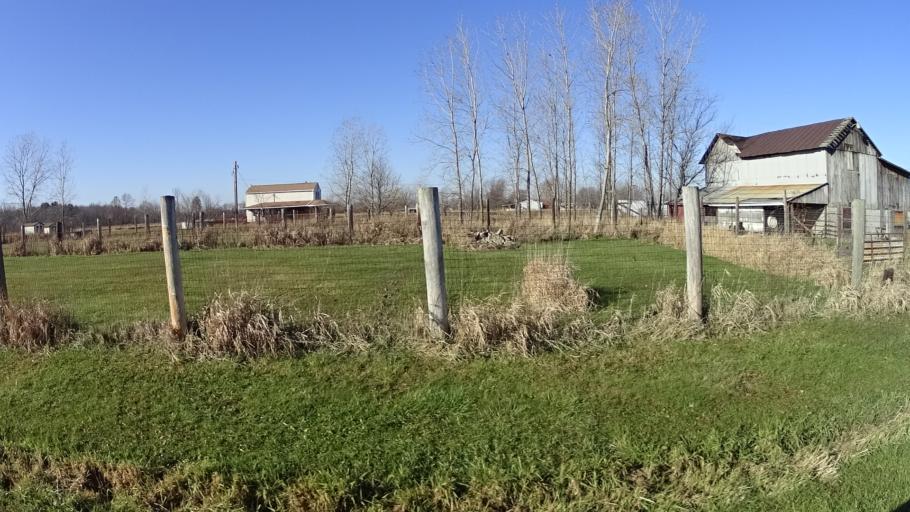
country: US
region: Ohio
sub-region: Lorain County
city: Wellington
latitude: 41.0993
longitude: -82.1808
